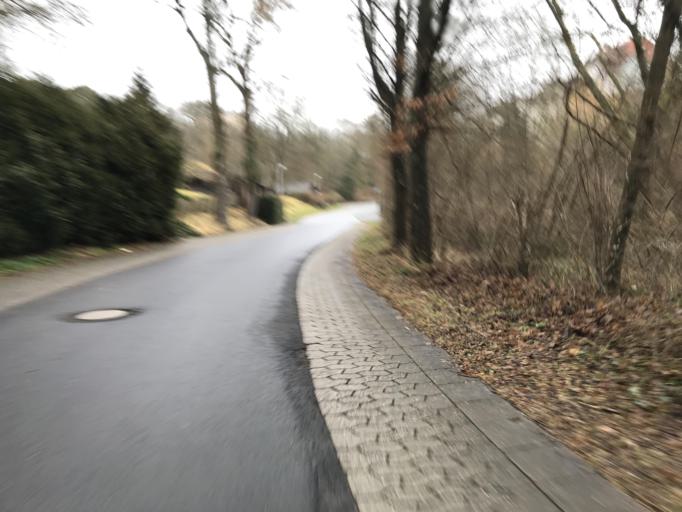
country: DE
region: Hesse
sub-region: Regierungsbezirk Kassel
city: Bad Wildungen
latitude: 51.1214
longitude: 9.1201
